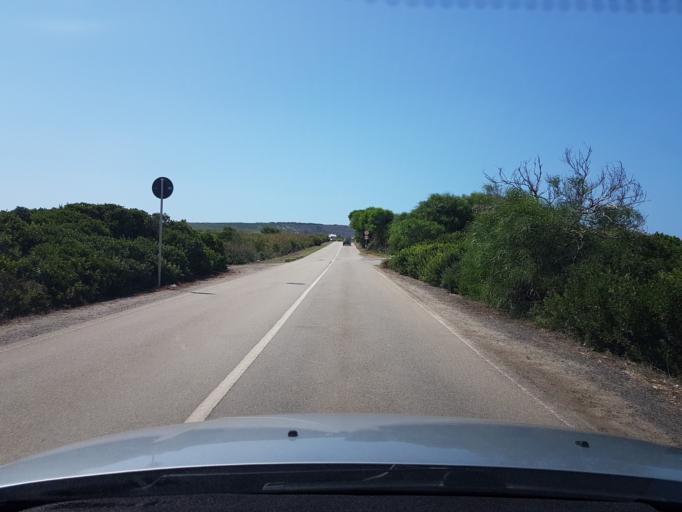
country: IT
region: Sardinia
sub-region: Provincia di Oristano
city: Riola Sardo
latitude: 40.0403
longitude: 8.4079
